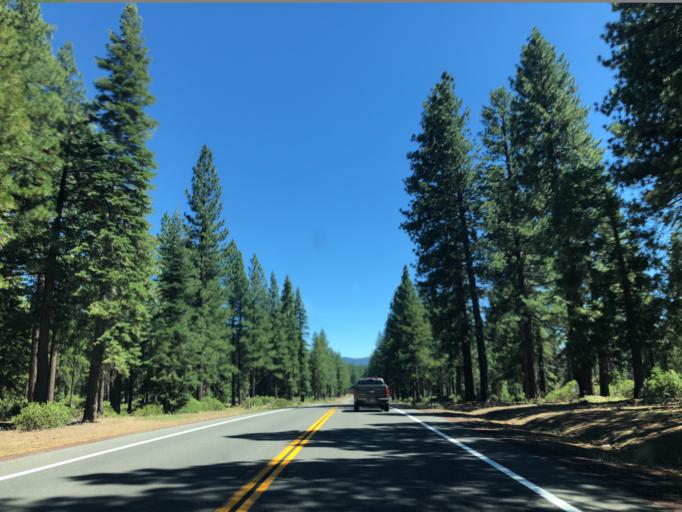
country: US
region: California
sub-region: Lassen County
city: Susanville
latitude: 40.4239
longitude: -120.7879
